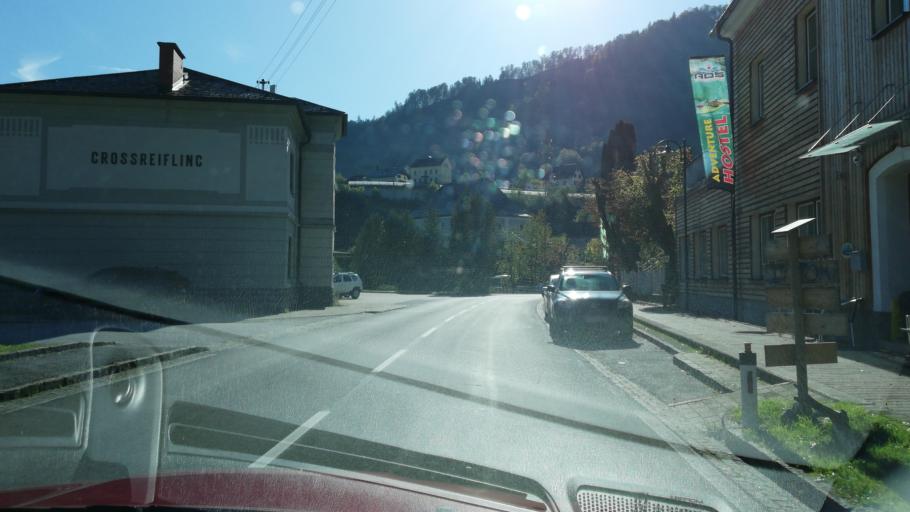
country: AT
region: Styria
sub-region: Politischer Bezirk Liezen
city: Landl
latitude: 47.6675
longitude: 14.7124
